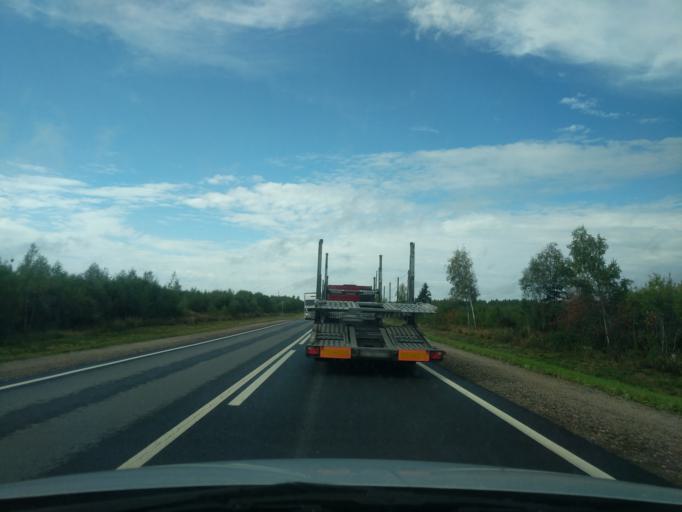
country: RU
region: Kostroma
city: Sudislavl'
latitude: 57.8199
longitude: 41.9220
